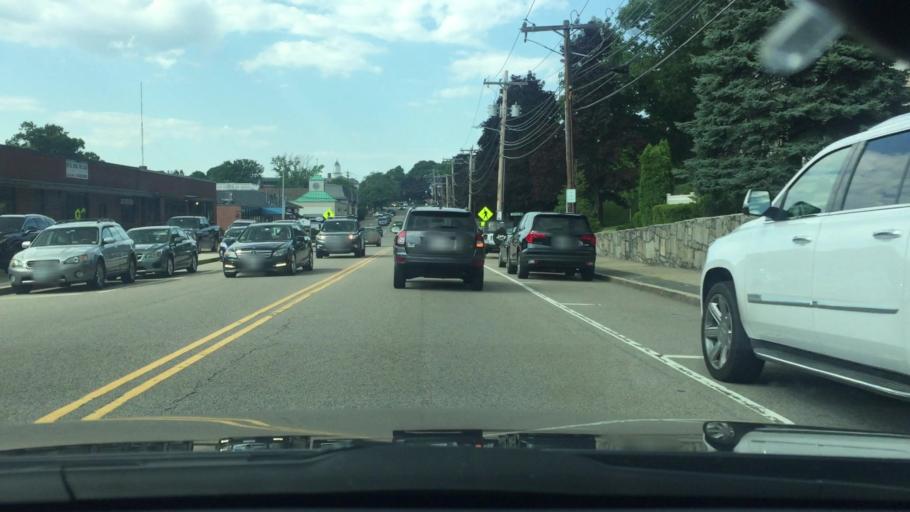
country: US
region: Massachusetts
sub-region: Norfolk County
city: Needham
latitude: 42.2846
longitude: -71.2359
